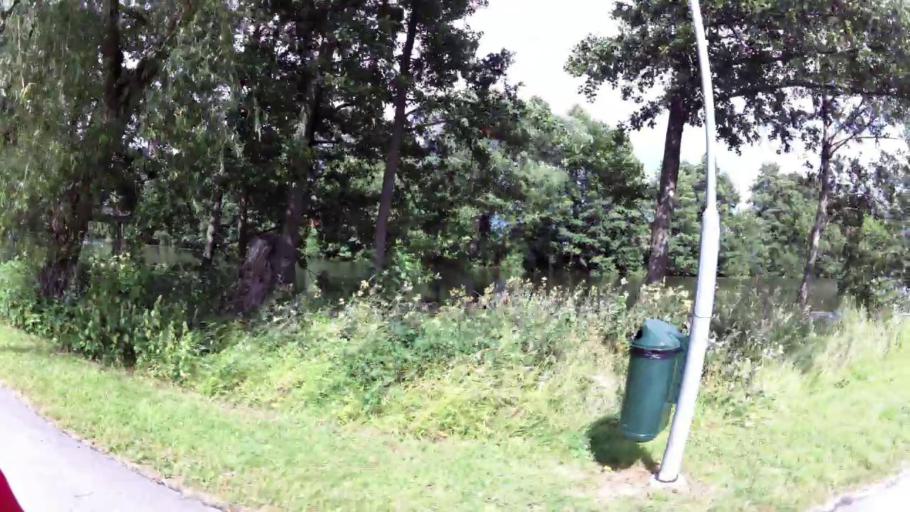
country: SE
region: OEstergoetland
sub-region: Linkopings Kommun
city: Linkoping
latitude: 58.3988
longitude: 15.6565
